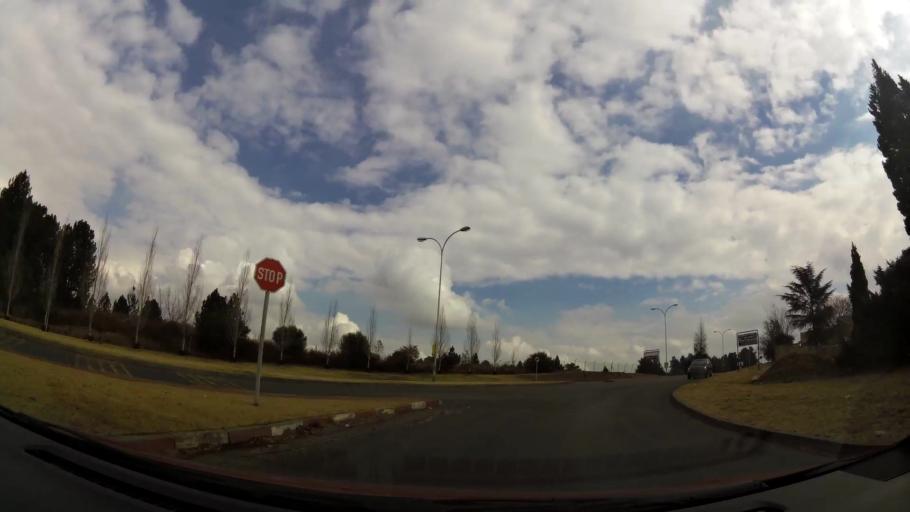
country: ZA
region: Gauteng
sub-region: Sedibeng District Municipality
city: Vanderbijlpark
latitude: -26.7434
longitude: 27.8539
